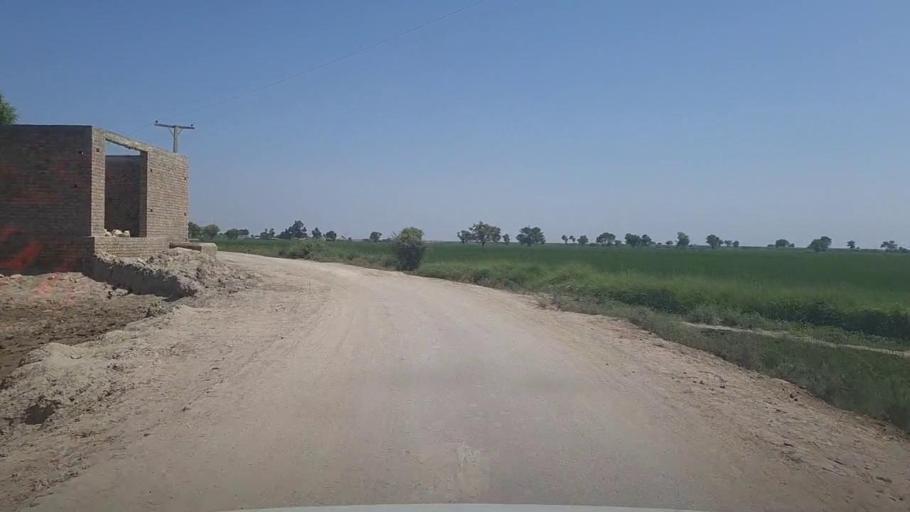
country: PK
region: Sindh
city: Kashmor
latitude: 28.2851
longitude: 69.4358
